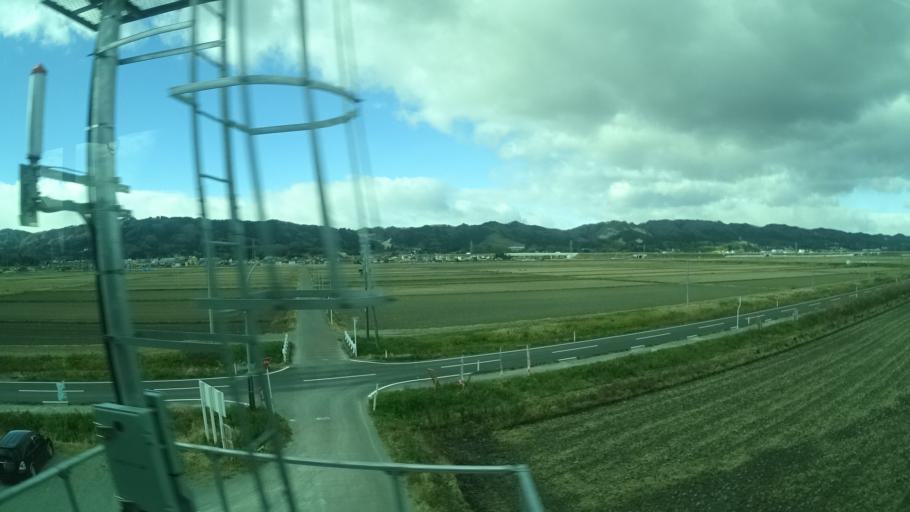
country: JP
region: Miyagi
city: Watari
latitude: 37.9765
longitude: 140.8864
